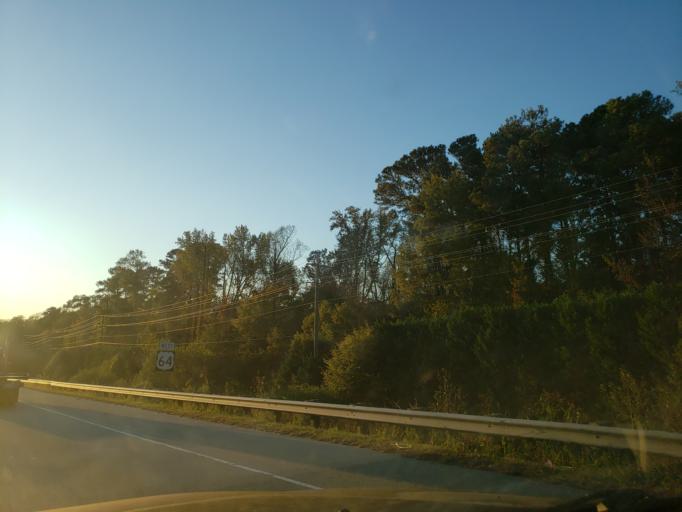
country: US
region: North Carolina
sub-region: Wake County
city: Apex
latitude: 35.7499
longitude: -78.8574
